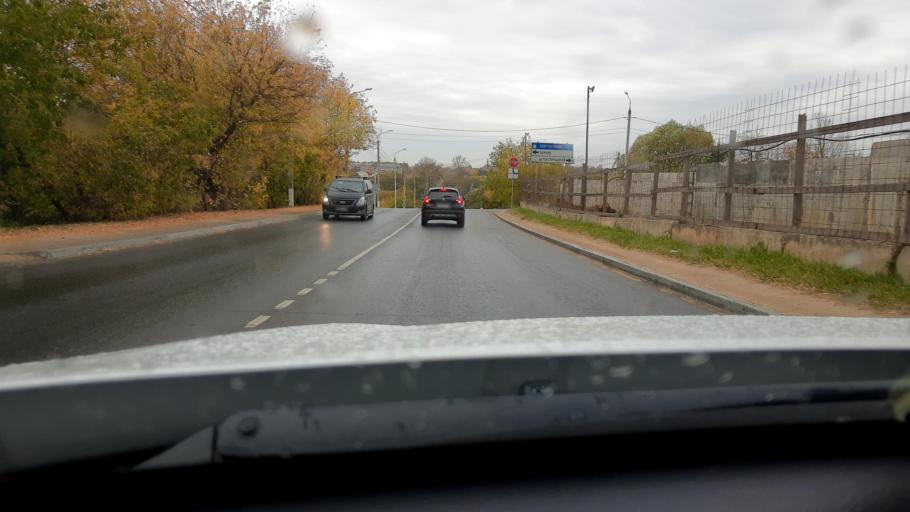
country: RU
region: Moskovskaya
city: Domodedovo
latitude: 55.4326
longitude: 37.7324
